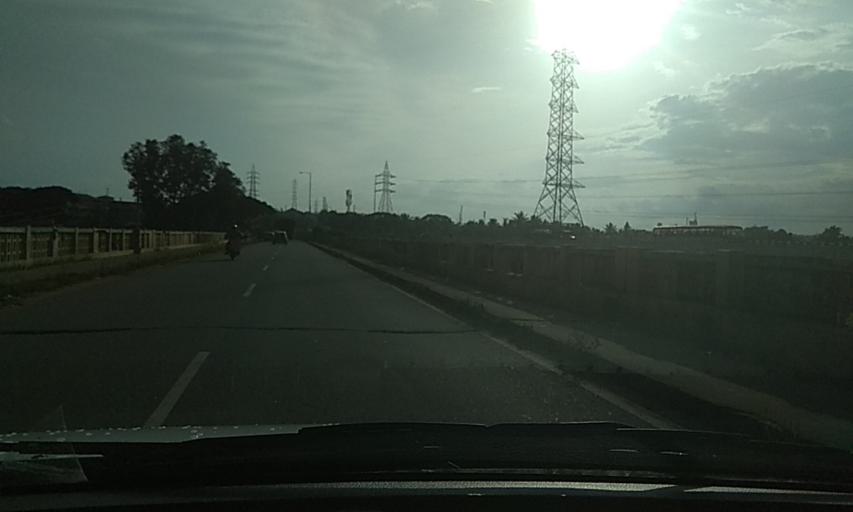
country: IN
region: Karnataka
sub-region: Mysore
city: Nanjangud
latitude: 12.1410
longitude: 76.6756
